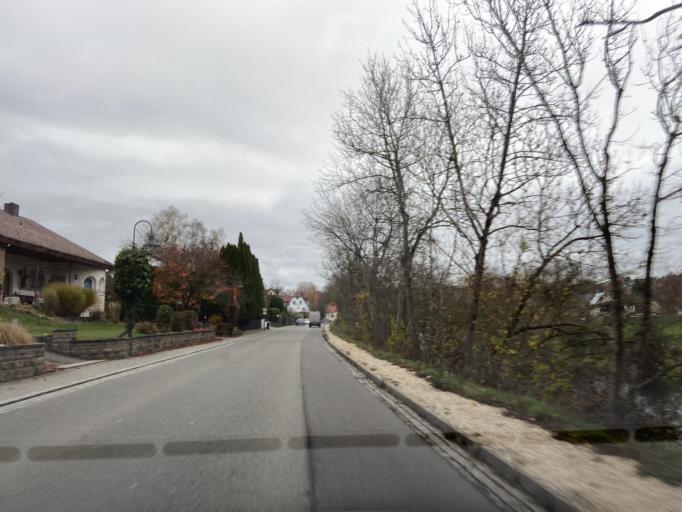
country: DE
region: Baden-Wuerttemberg
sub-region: Tuebingen Region
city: Sigmaringendorf
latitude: 48.0634
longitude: 9.2614
